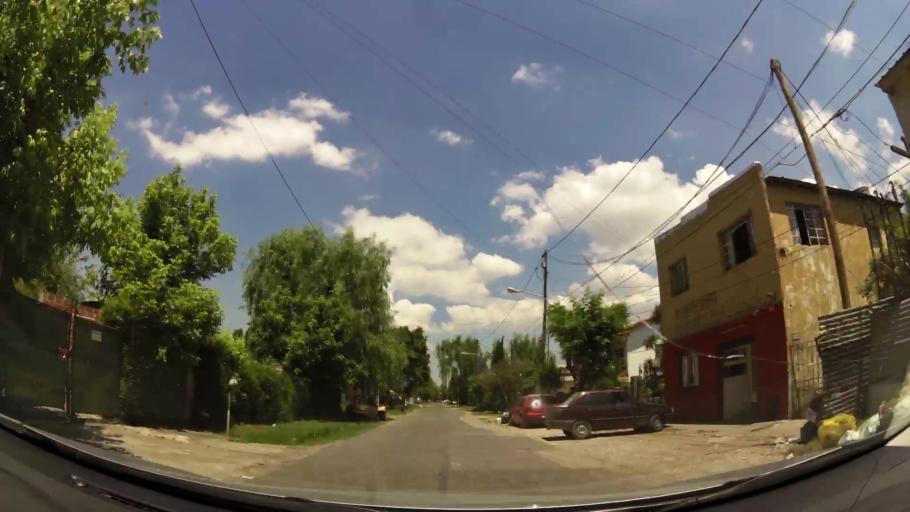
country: AR
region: Buenos Aires
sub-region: Partido de Tigre
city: Tigre
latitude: -34.4108
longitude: -58.5962
